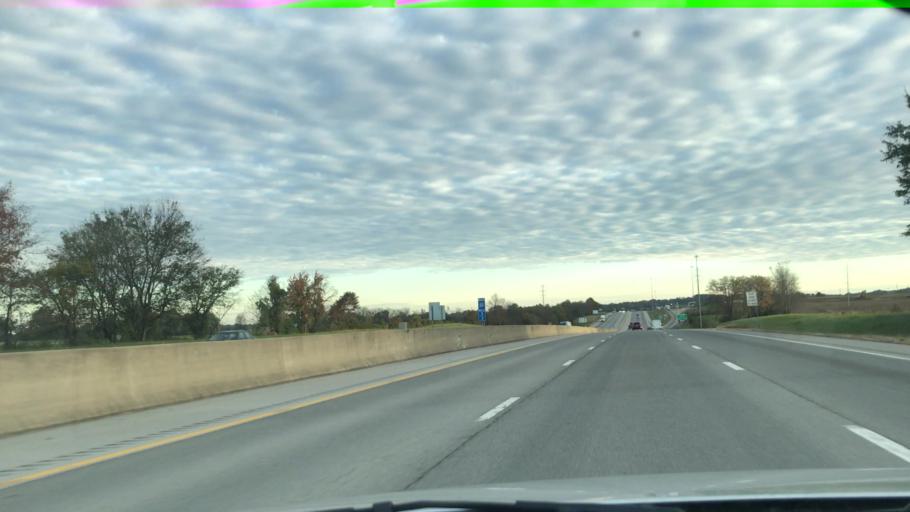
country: US
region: Kentucky
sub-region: Simpson County
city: Franklin
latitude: 36.6790
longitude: -86.5448
